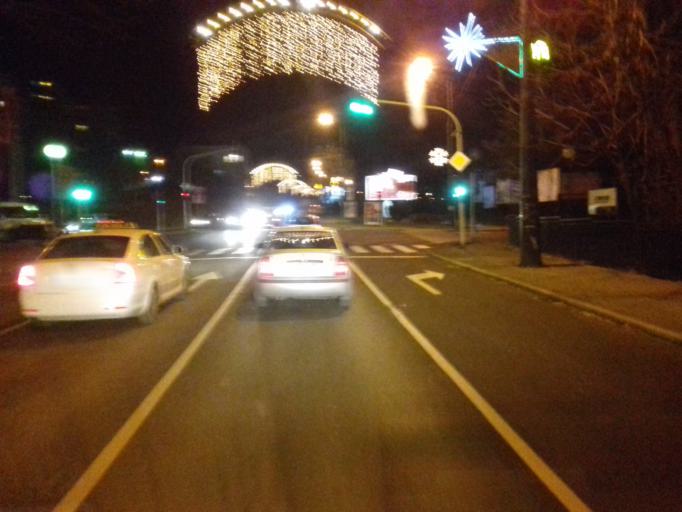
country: BA
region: Federation of Bosnia and Herzegovina
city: Kobilja Glava
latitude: 43.8681
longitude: 18.4090
